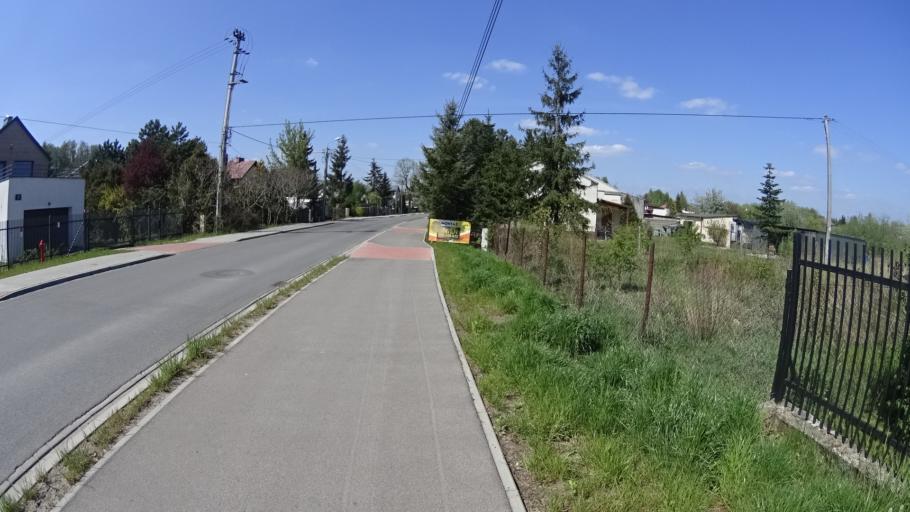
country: PL
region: Masovian Voivodeship
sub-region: Powiat warszawski zachodni
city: Hornowek
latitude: 52.2688
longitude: 20.8082
